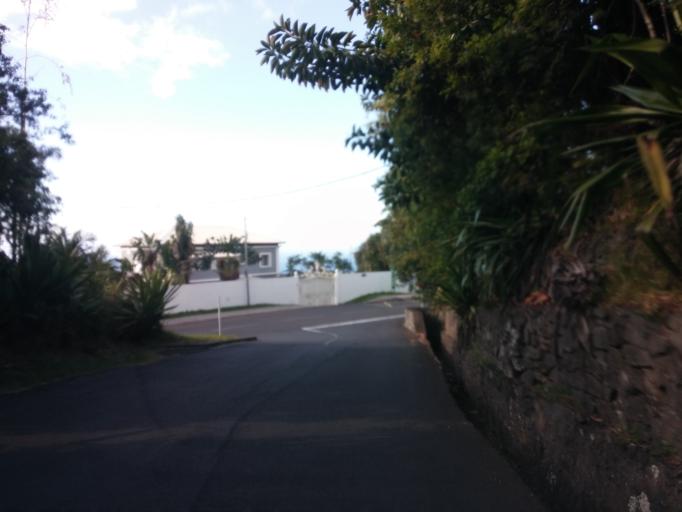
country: RE
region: Reunion
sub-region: Reunion
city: Saint-Denis
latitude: -20.8832
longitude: 55.4284
